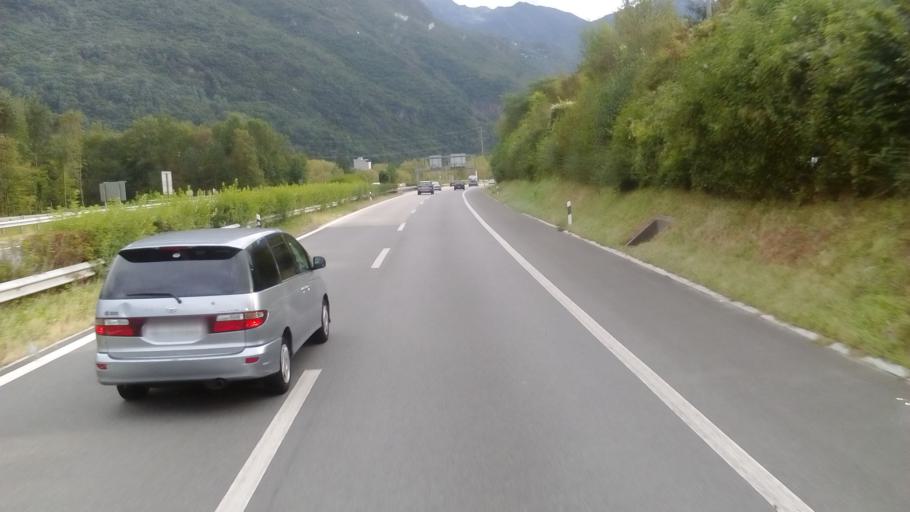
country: CH
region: Ticino
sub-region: Bellinzona District
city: Bellinzona
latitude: 46.2187
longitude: 9.0362
